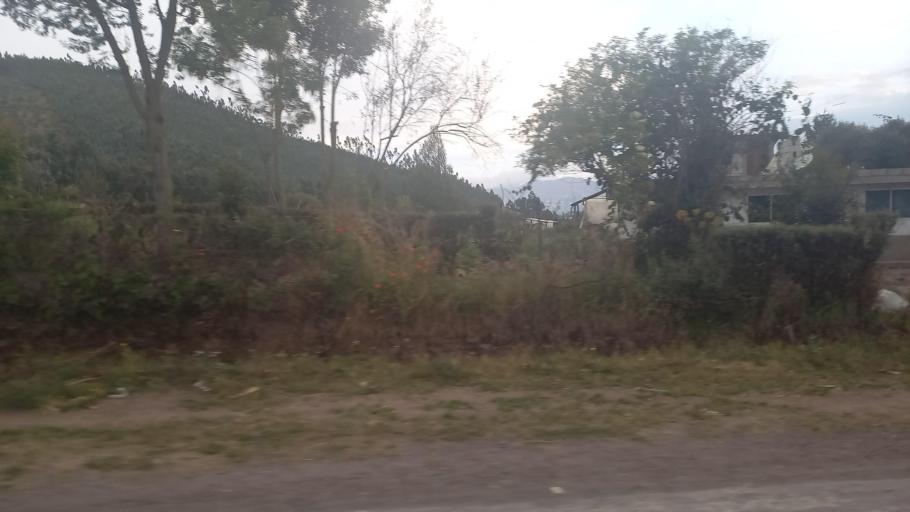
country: EC
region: Pichincha
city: Cayambe
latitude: 0.0707
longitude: -78.1166
